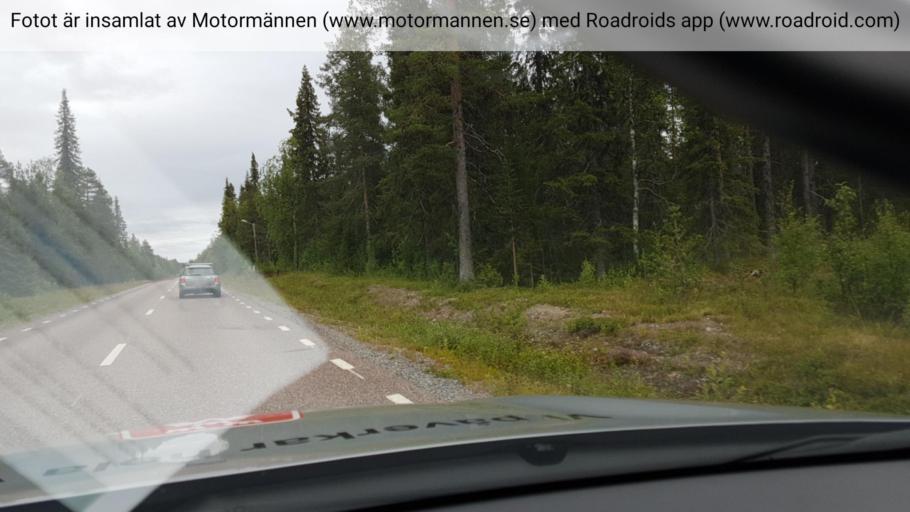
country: SE
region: Norrbotten
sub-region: Gallivare Kommun
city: Gaellivare
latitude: 67.0548
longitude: 21.5903
